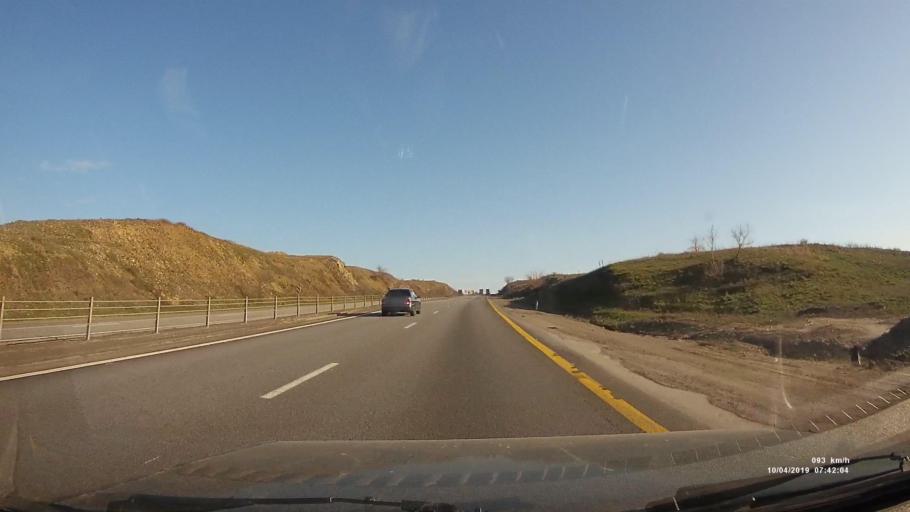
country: RU
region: Rostov
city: Likhoy
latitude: 48.1437
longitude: 40.2599
